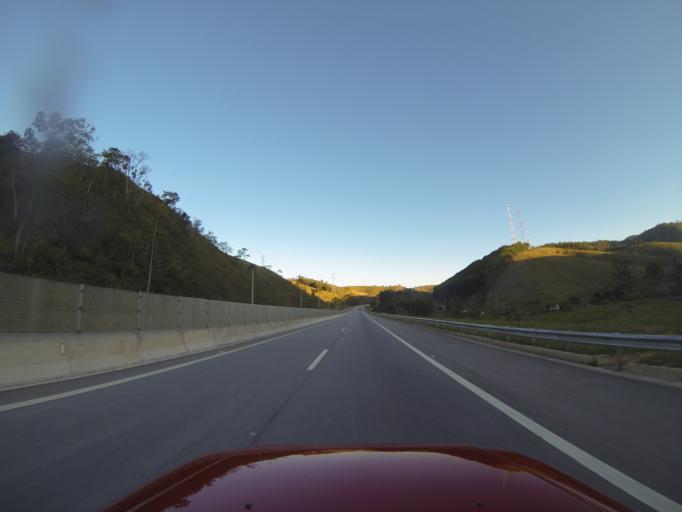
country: BR
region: Sao Paulo
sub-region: Caraguatatuba
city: Caraguatatuba
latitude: -23.4639
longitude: -45.5879
